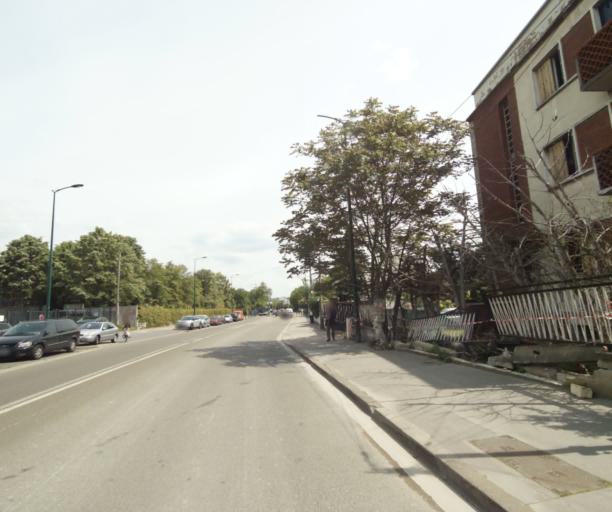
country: FR
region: Ile-de-France
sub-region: Departement des Hauts-de-Seine
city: Colombes
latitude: 48.9227
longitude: 2.2341
